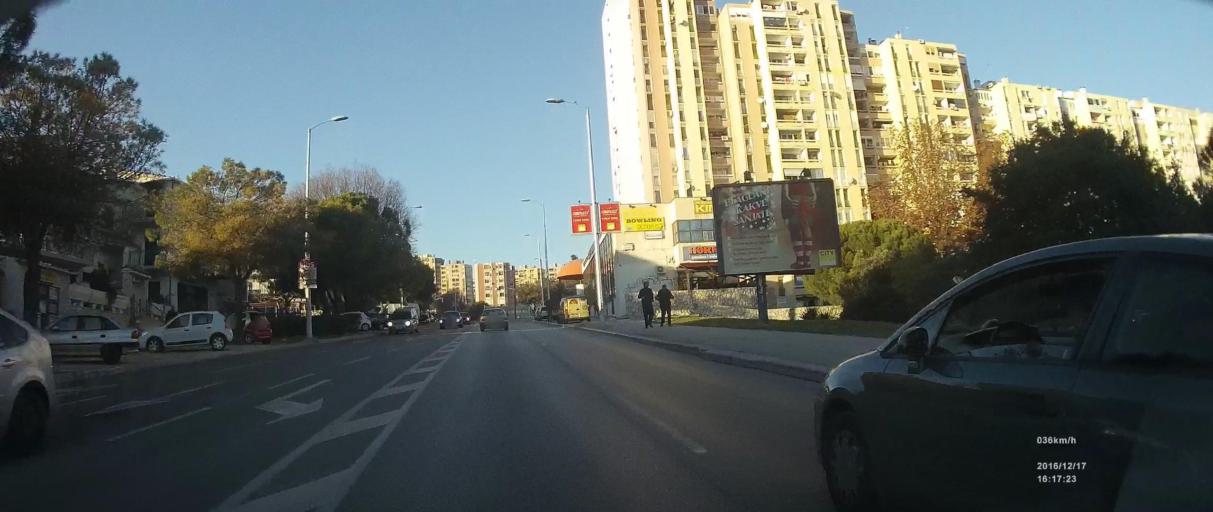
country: HR
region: Splitsko-Dalmatinska
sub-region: Grad Split
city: Split
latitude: 43.5081
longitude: 16.4642
